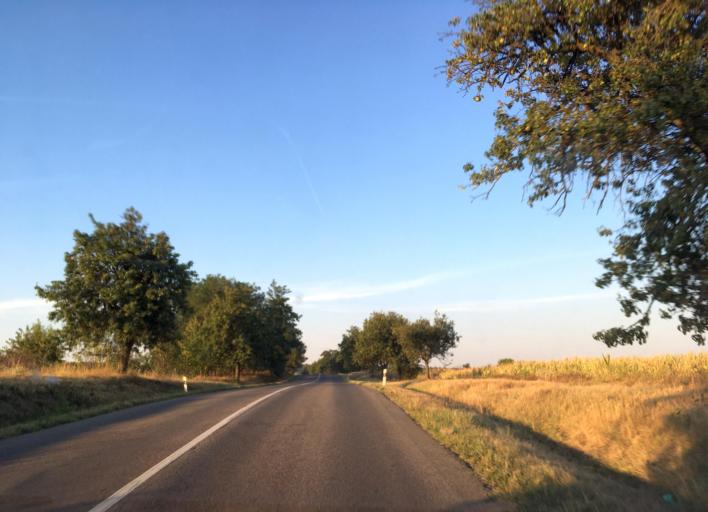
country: HU
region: Komarom-Esztergom
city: Neszmely
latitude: 47.8114
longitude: 18.3411
